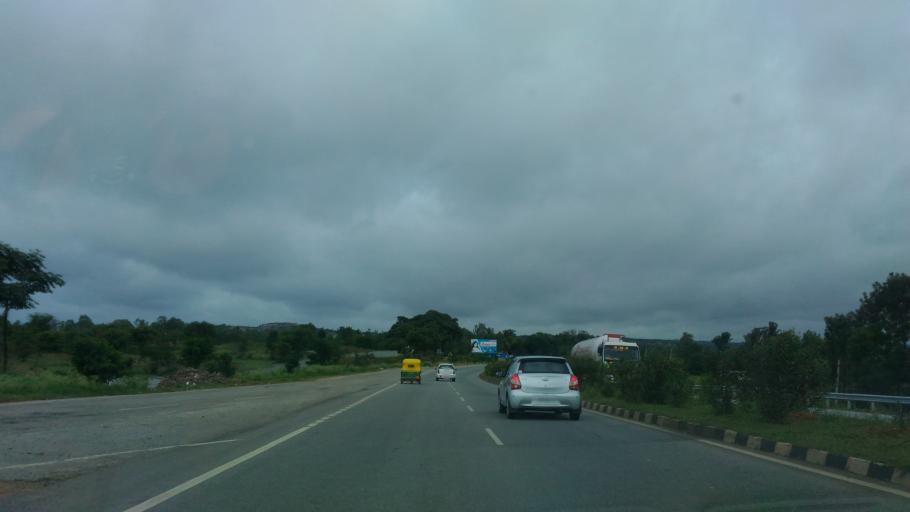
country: IN
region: Karnataka
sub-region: Bangalore Rural
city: Nelamangala
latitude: 13.0608
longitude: 77.3387
